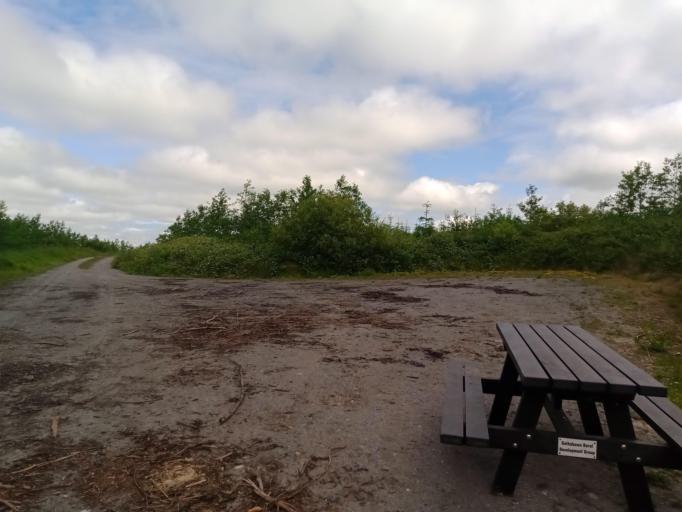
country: IE
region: Leinster
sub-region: Kilkenny
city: Ballyragget
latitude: 52.7912
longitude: -7.4453
